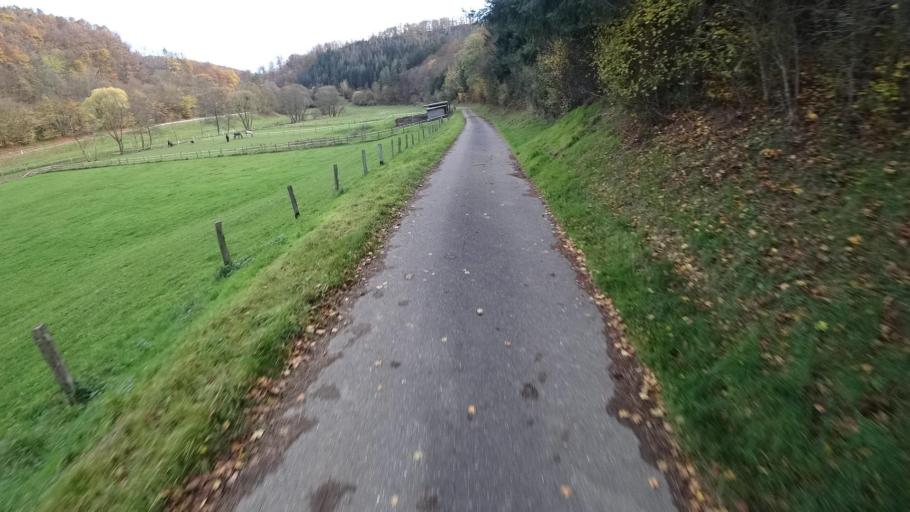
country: DE
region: Rheinland-Pfalz
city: Lind
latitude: 50.4861
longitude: 6.9082
